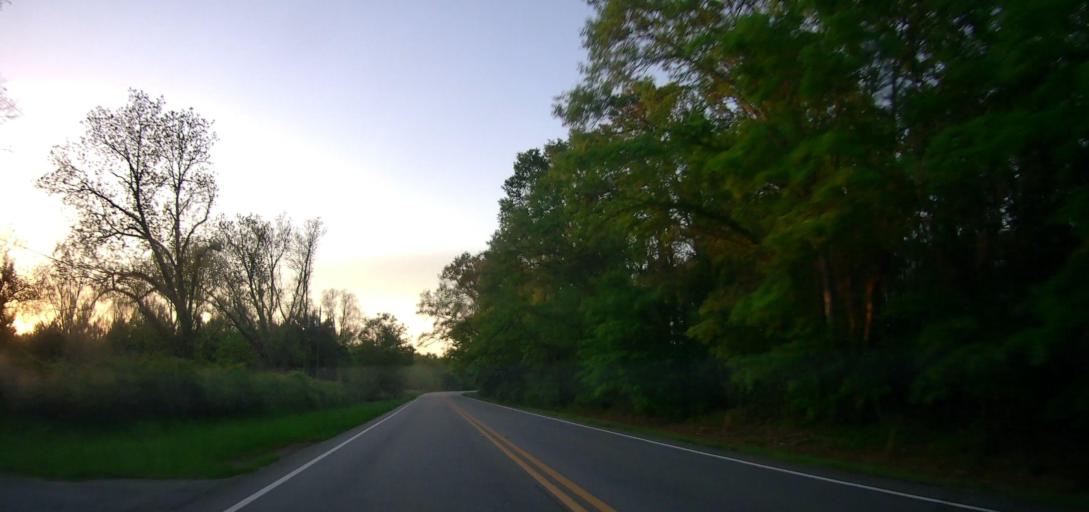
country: US
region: Georgia
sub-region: Marion County
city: Buena Vista
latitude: 32.3525
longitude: -84.5357
